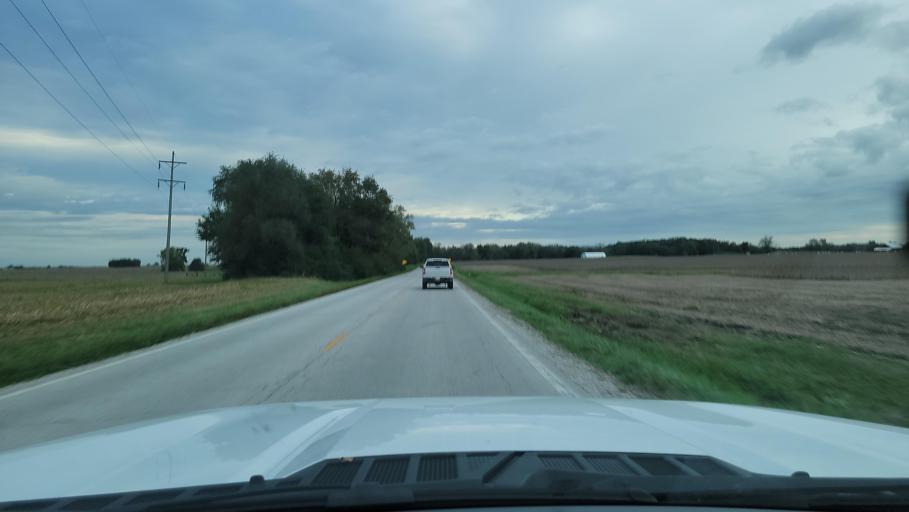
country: US
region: Illinois
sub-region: Schuyler County
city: Rushville
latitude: 40.1475
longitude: -90.5571
